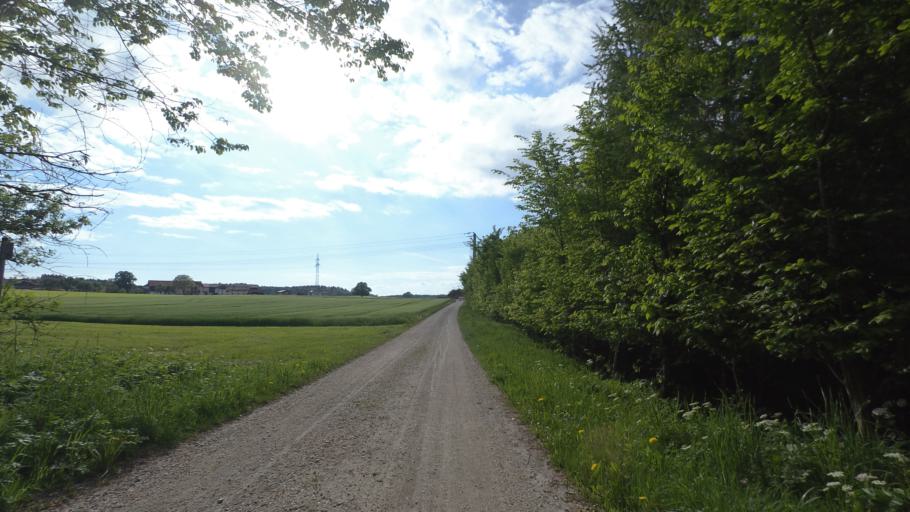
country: DE
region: Bavaria
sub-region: Upper Bavaria
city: Nussdorf
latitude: 47.8984
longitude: 12.6112
